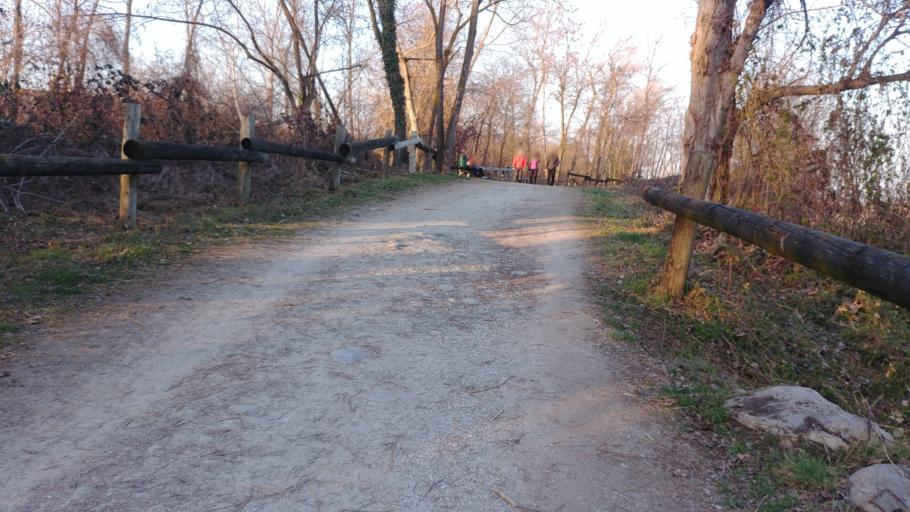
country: IT
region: Piedmont
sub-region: Provincia di Cuneo
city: Cuneo
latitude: 44.3618
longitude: 7.5371
